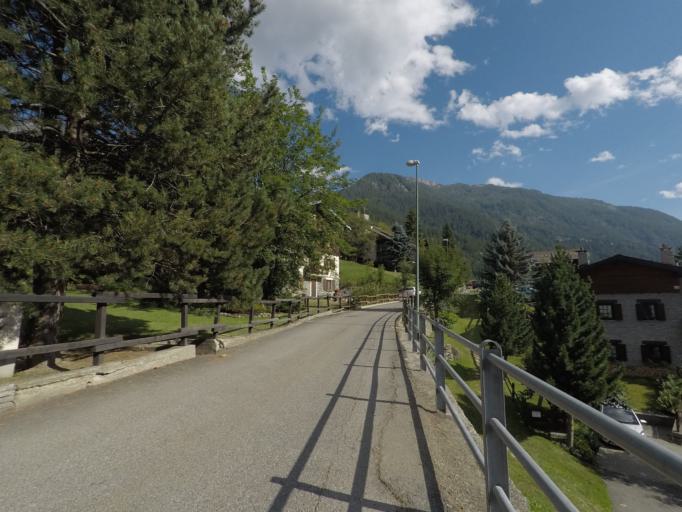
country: IT
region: Aosta Valley
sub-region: Valle d'Aosta
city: Valtournenche
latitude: 45.8770
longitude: 7.6254
